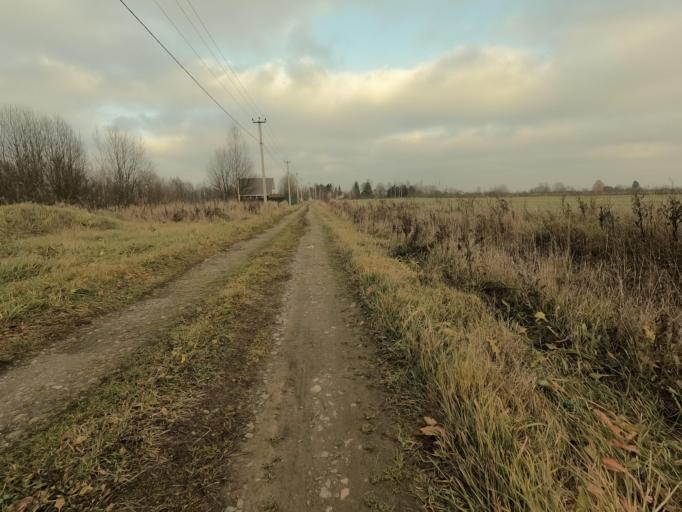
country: RU
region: Leningrad
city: Mga
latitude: 59.7548
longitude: 31.0624
